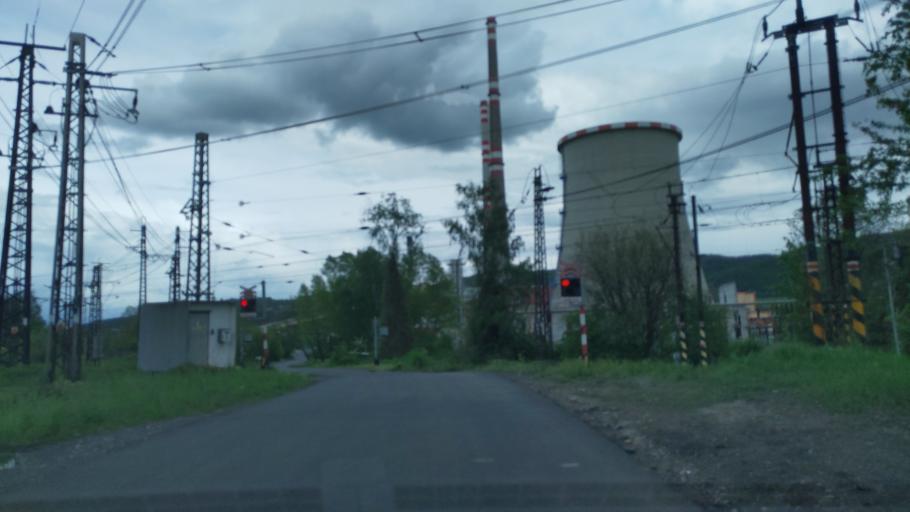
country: CZ
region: Ustecky
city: Trmice
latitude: 50.6462
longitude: 13.9808
